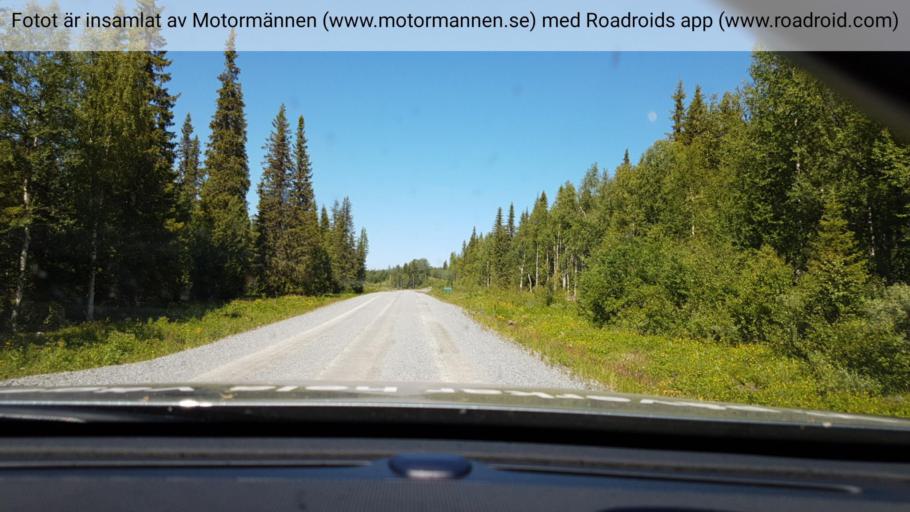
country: SE
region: Vaesterbotten
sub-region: Vilhelmina Kommun
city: Sjoberg
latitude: 64.7308
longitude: 15.7820
